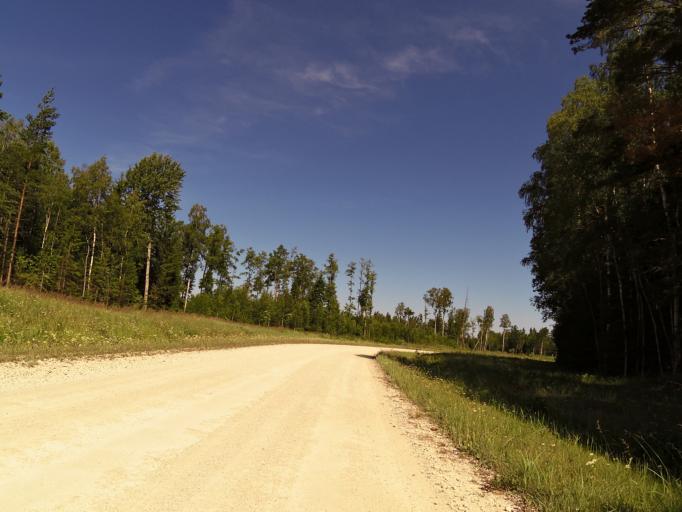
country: EE
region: Hiiumaa
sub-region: Kaerdla linn
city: Kardla
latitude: 58.9258
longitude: 22.3679
